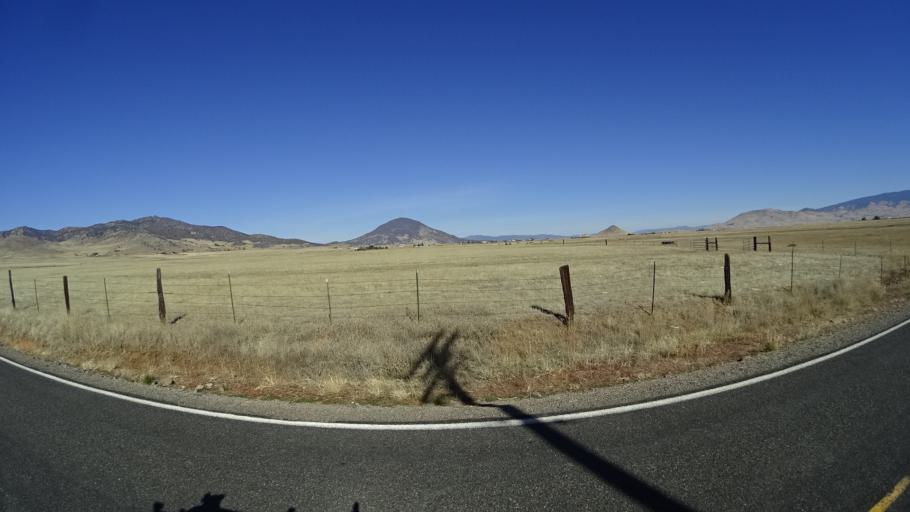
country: US
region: California
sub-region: Siskiyou County
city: Montague
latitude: 41.7706
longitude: -122.4973
